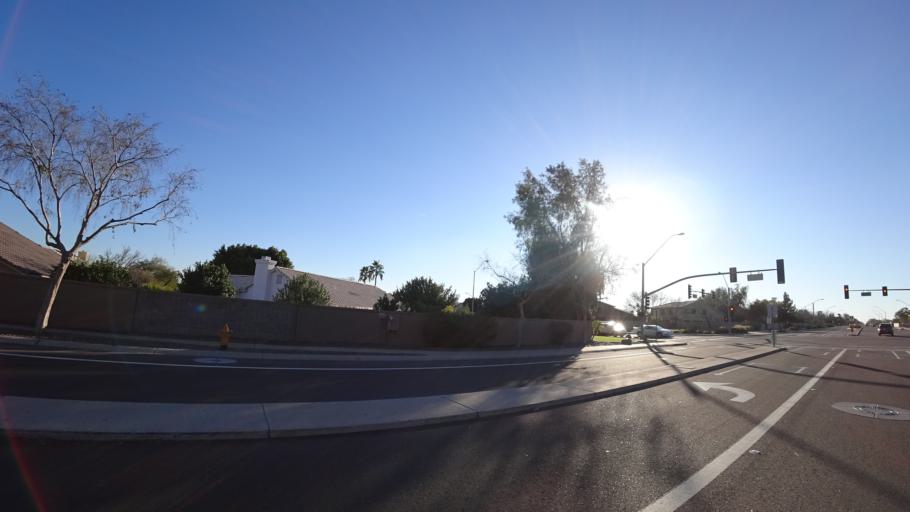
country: US
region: Arizona
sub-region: Maricopa County
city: Peoria
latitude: 33.6819
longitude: -112.2025
